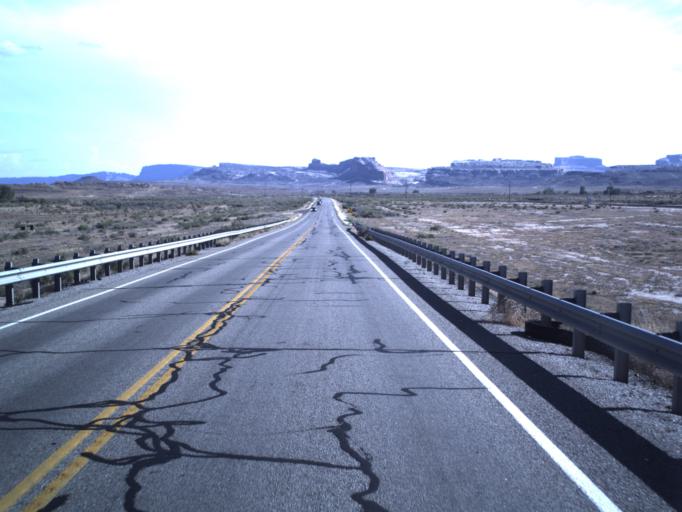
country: US
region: Utah
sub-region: Grand County
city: Moab
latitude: 38.7531
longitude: -109.7396
